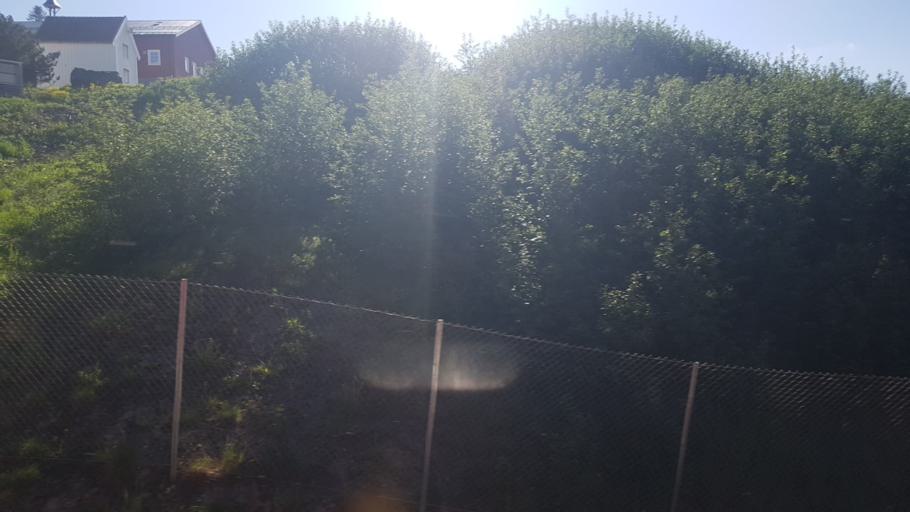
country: NO
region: Sor-Trondelag
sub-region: Melhus
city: Melhus
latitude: 63.3246
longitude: 10.3275
